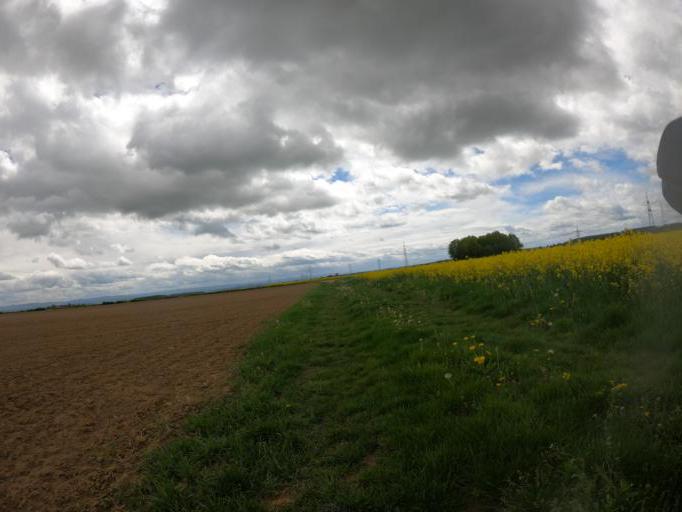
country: DE
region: Baden-Wuerttemberg
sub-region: Regierungsbezirk Stuttgart
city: Oberjettingen
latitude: 48.5797
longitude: 8.7946
